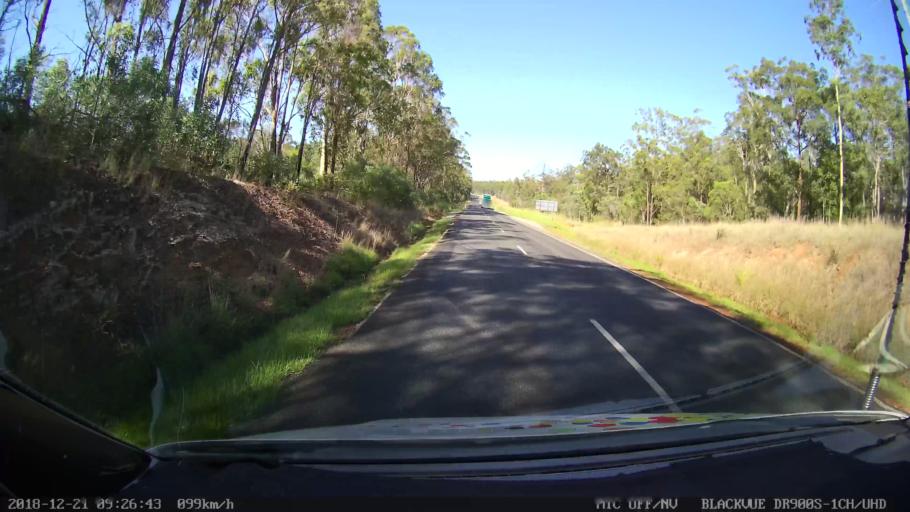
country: AU
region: New South Wales
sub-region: Clarence Valley
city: Maclean
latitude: -29.3958
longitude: 152.9988
